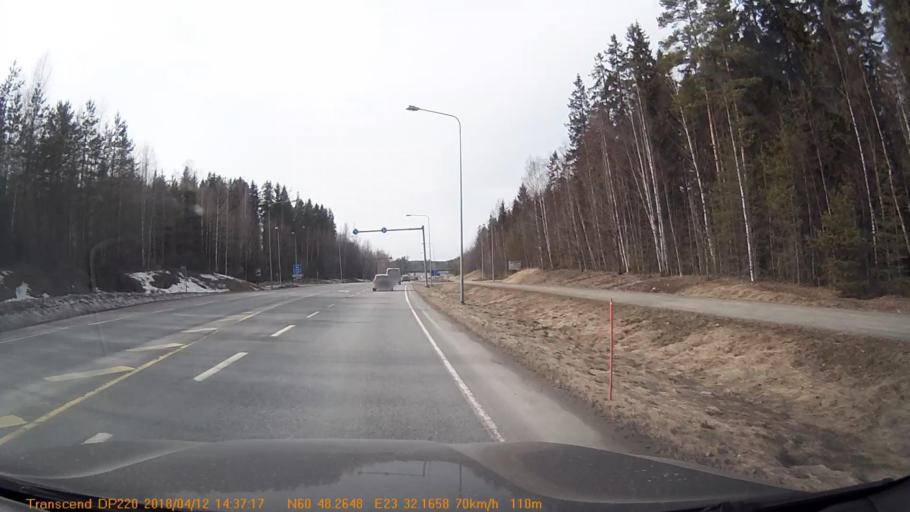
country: FI
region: Haeme
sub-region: Forssa
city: Jokioinen
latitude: 60.8050
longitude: 23.5337
